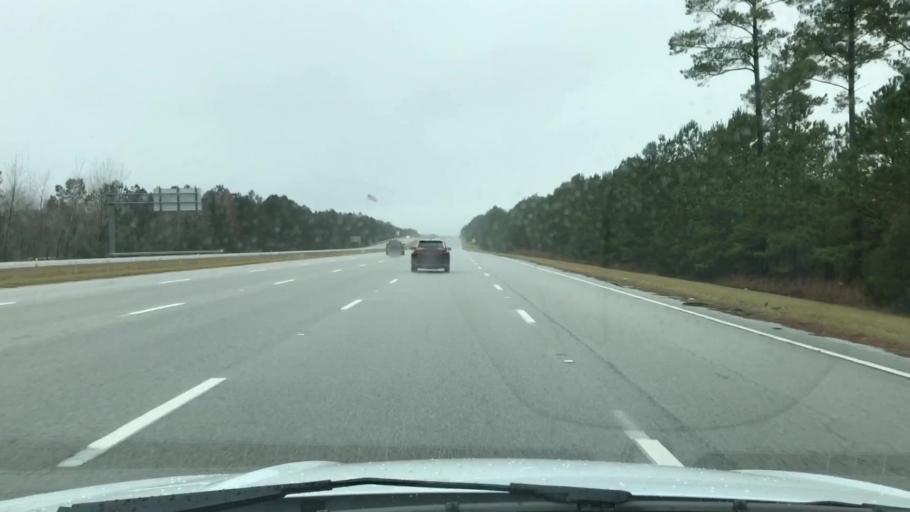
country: US
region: South Carolina
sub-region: Horry County
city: Myrtle Beach
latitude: 33.7524
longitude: -78.8606
